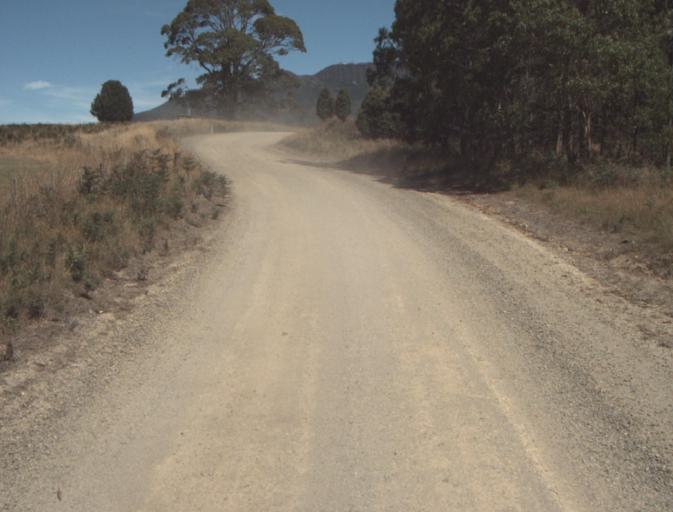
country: AU
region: Tasmania
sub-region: Dorset
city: Scottsdale
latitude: -41.3264
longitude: 147.4444
